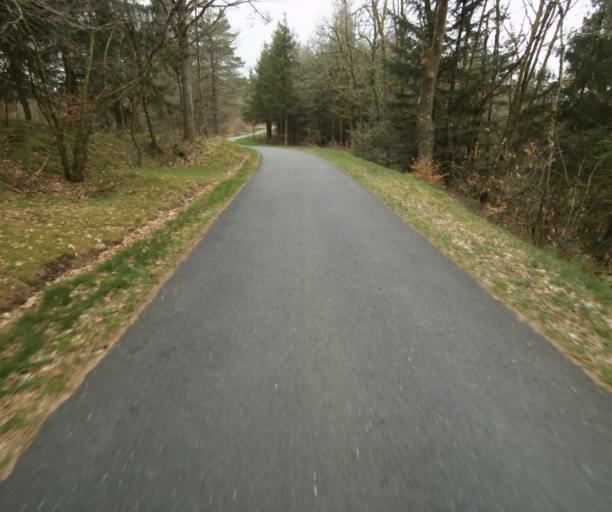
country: FR
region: Limousin
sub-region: Departement de la Correze
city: Correze
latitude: 45.3051
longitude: 1.9078
